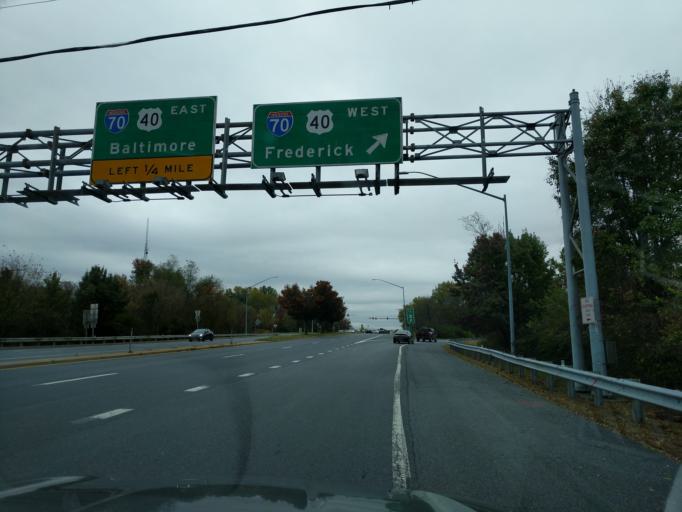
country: US
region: Maryland
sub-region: Frederick County
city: Linganore
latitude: 39.3852
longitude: -77.2601
